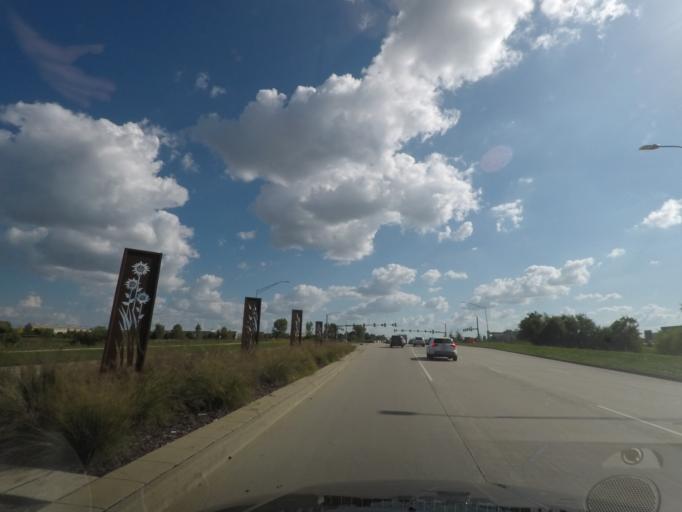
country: US
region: Iowa
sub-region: Dallas County
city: Waukee
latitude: 41.5747
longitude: -93.8093
